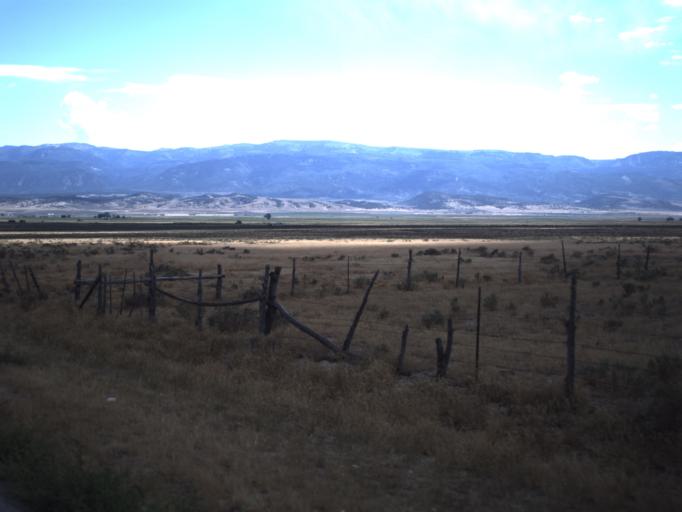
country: US
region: Utah
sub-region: Sanpete County
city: Moroni
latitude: 39.4753
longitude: -111.6273
